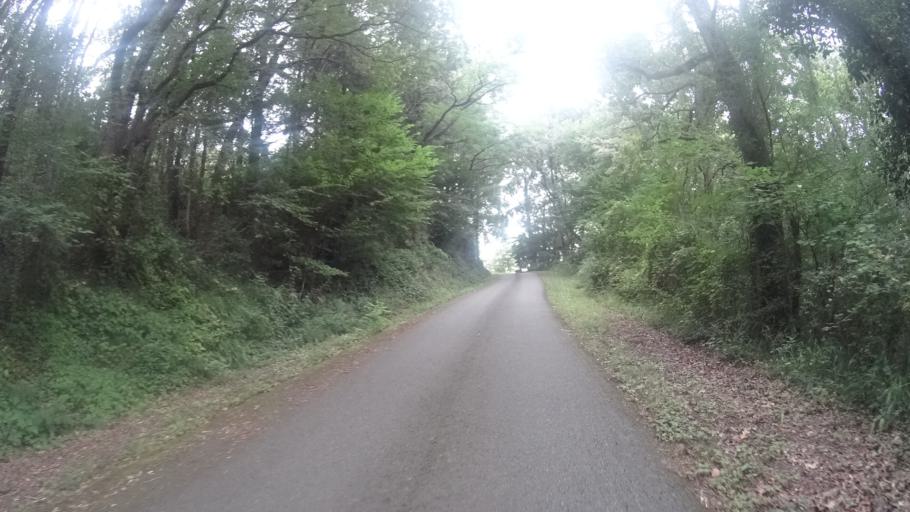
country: FR
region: Aquitaine
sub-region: Departement des Pyrenees-Atlantiques
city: Mont
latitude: 43.4833
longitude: -0.6946
